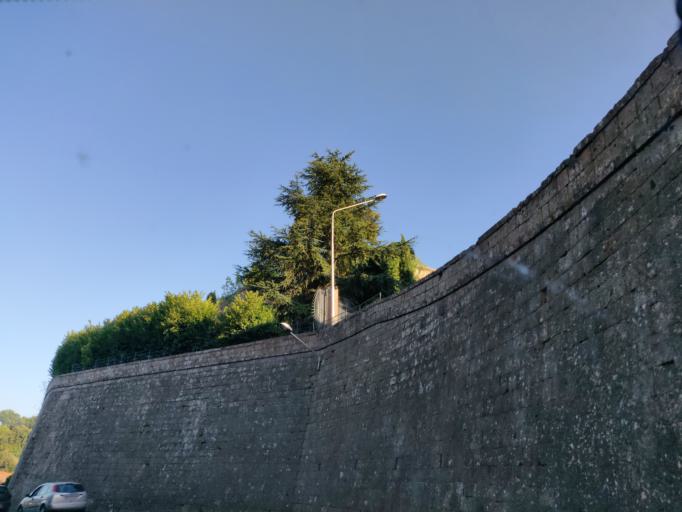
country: IT
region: Latium
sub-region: Provincia di Viterbo
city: Acquapendente
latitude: 42.7426
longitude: 11.8637
